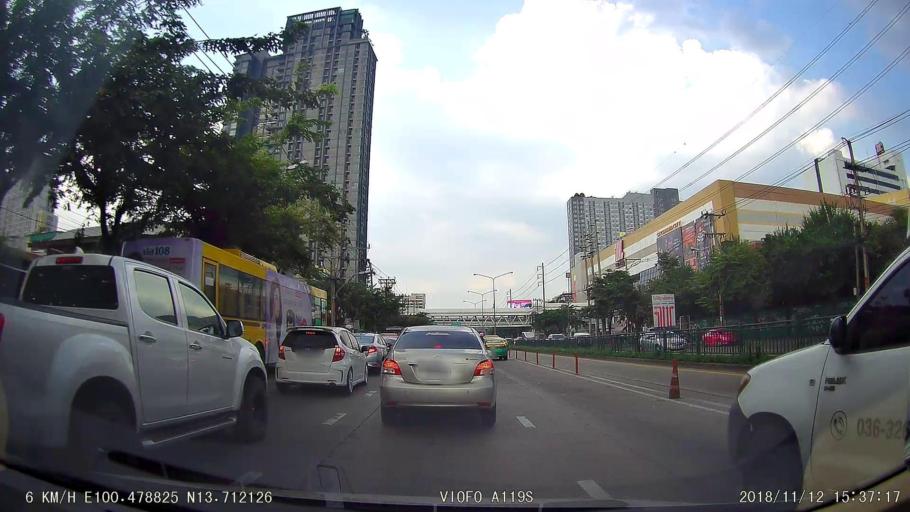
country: TH
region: Bangkok
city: Bangkok Yai
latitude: 13.7122
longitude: 100.4788
